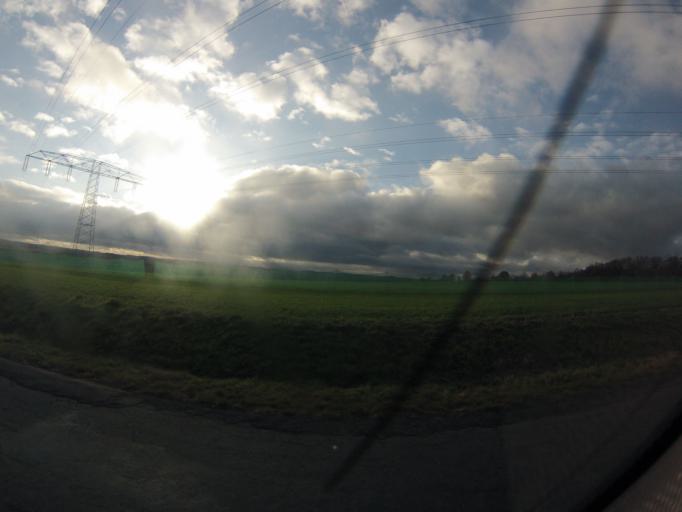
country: DE
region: Thuringia
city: Nobdenitz
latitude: 50.8662
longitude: 12.2966
